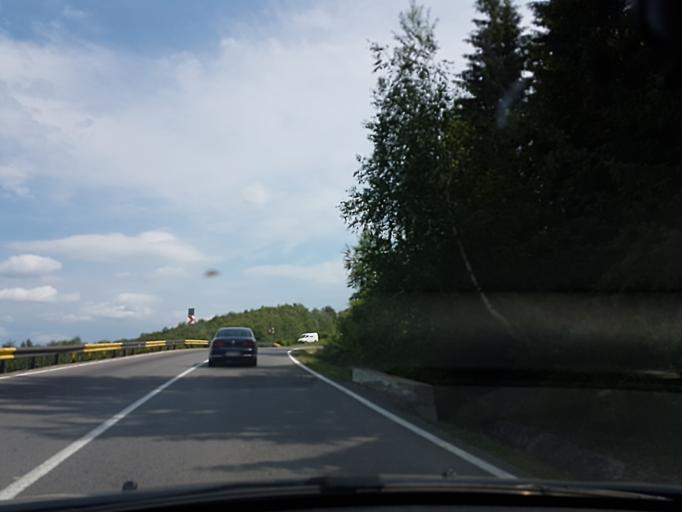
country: RO
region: Prahova
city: Maneciu
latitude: 45.3349
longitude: 25.9665
